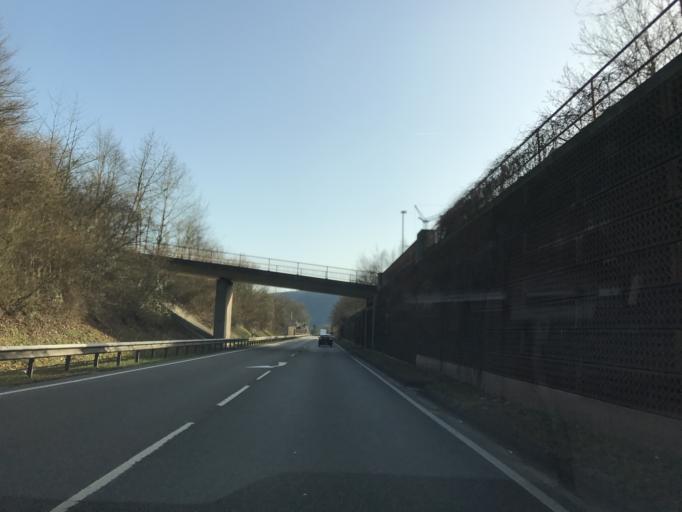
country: DE
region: Rheinland-Pfalz
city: Rheinbrohl
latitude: 50.4961
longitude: 7.3349
